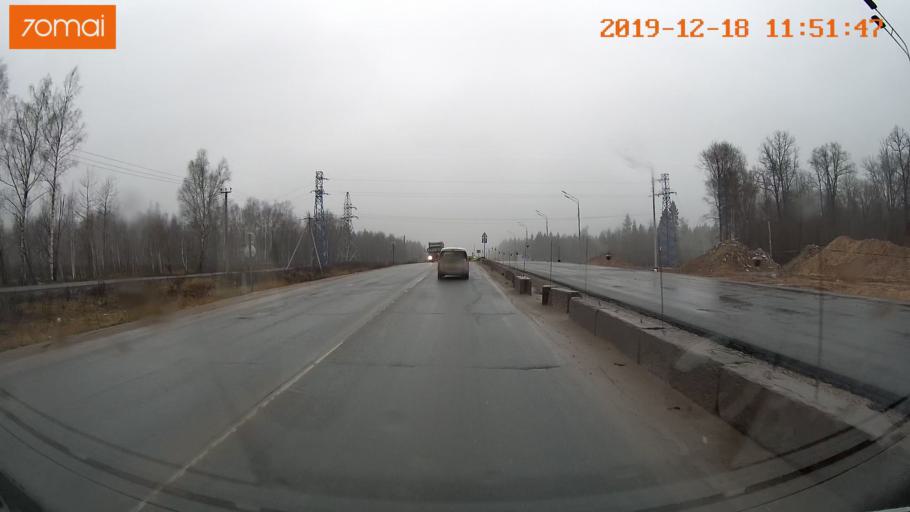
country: RU
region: Moskovskaya
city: Yershovo
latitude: 55.7957
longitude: 36.9213
